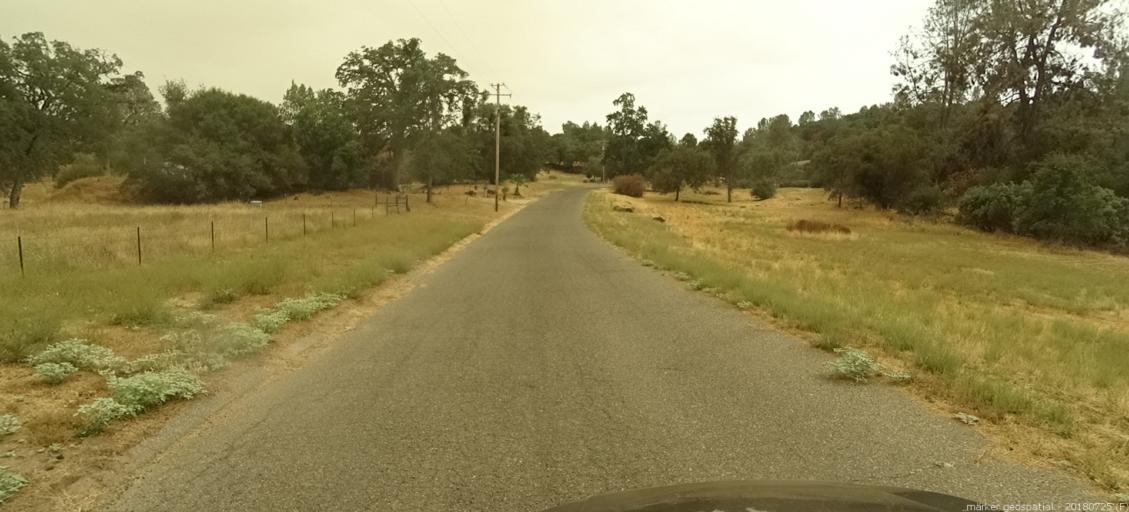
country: US
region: California
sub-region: Madera County
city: Coarsegold
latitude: 37.1974
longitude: -119.6735
